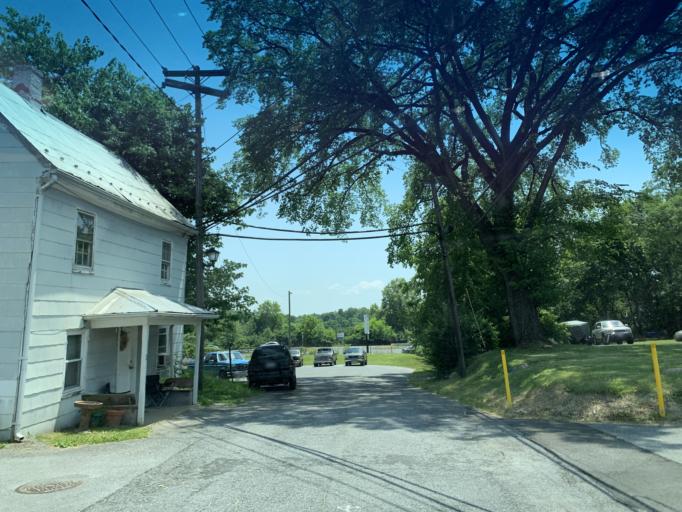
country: US
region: Maryland
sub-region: Frederick County
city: Green Valley
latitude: 39.3821
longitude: -77.2696
